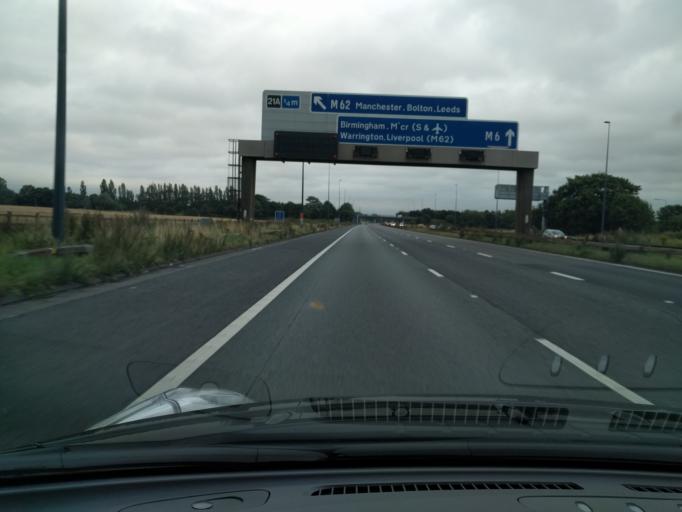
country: GB
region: England
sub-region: Warrington
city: Croft
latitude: 53.4326
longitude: -2.5677
